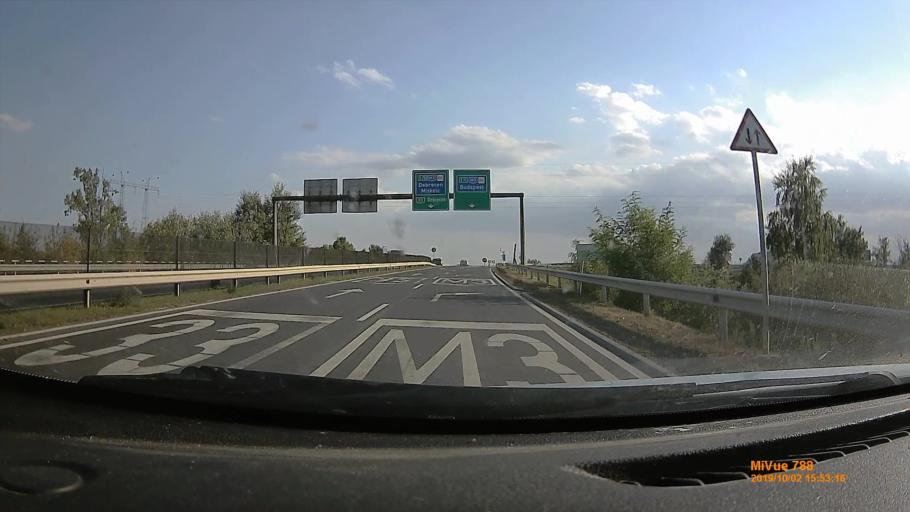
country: HU
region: Heves
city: Fuzesabony
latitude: 47.7331
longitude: 20.4129
